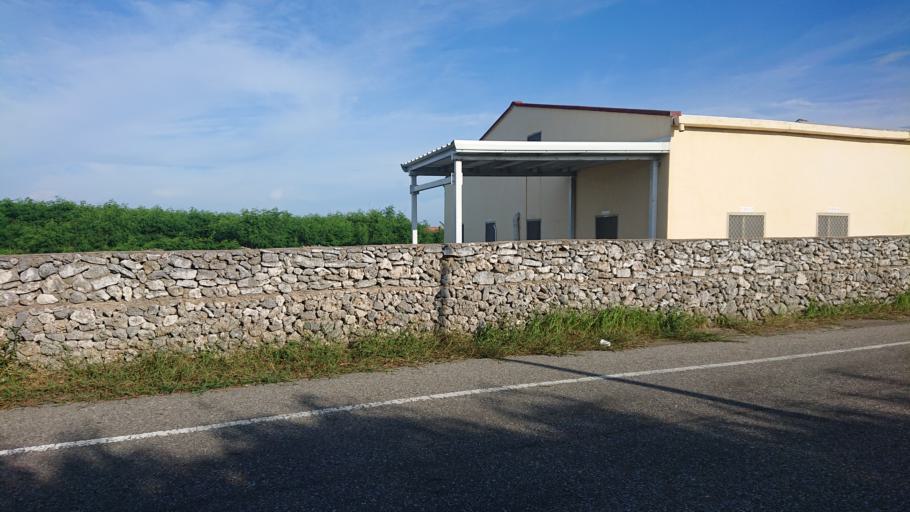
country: TW
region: Taiwan
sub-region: Penghu
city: Ma-kung
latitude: 23.6059
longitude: 119.5182
